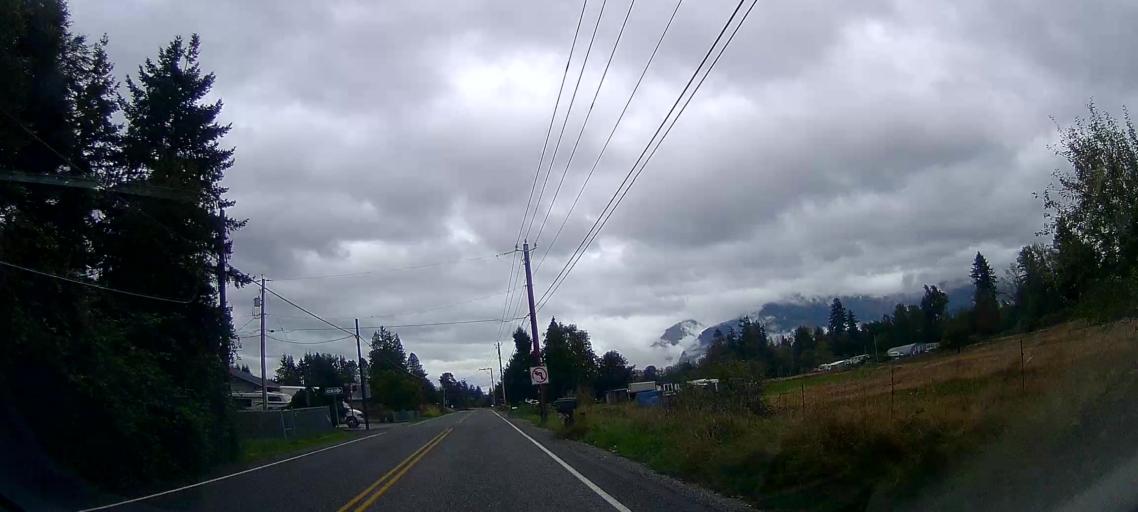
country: US
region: Washington
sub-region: Skagit County
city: Sedro-Woolley
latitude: 48.5264
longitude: -122.0905
